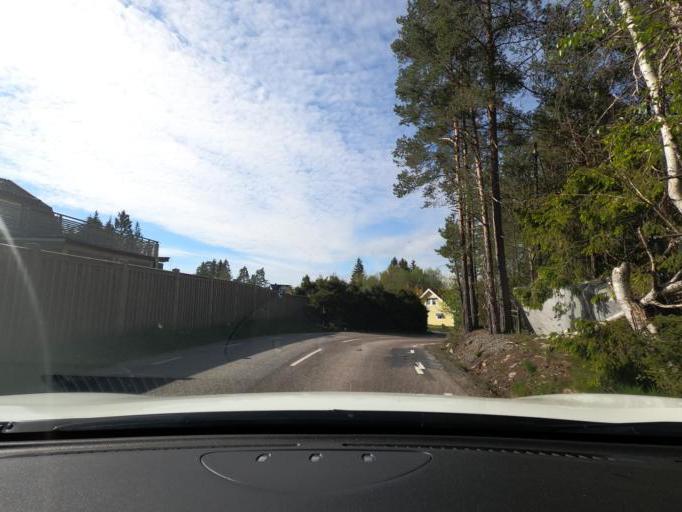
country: SE
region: Vaestra Goetaland
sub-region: Harryda Kommun
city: Landvetter
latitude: 57.6713
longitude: 12.2430
